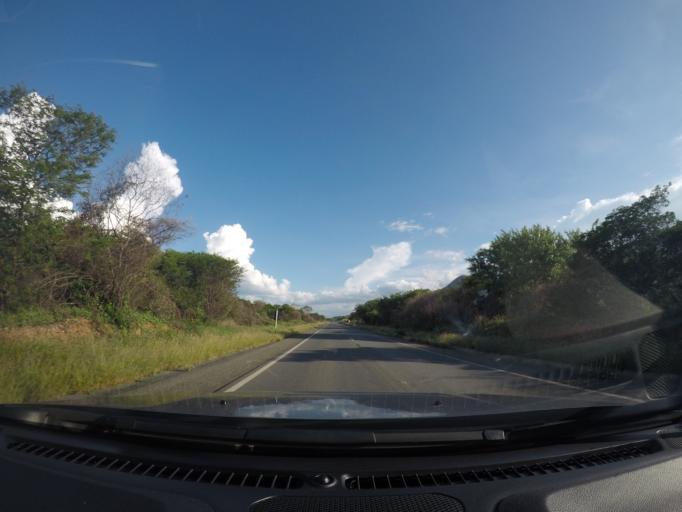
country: BR
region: Bahia
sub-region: Oliveira Dos Brejinhos
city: Oliveira dos Brejinhos
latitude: -12.0527
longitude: -42.9671
